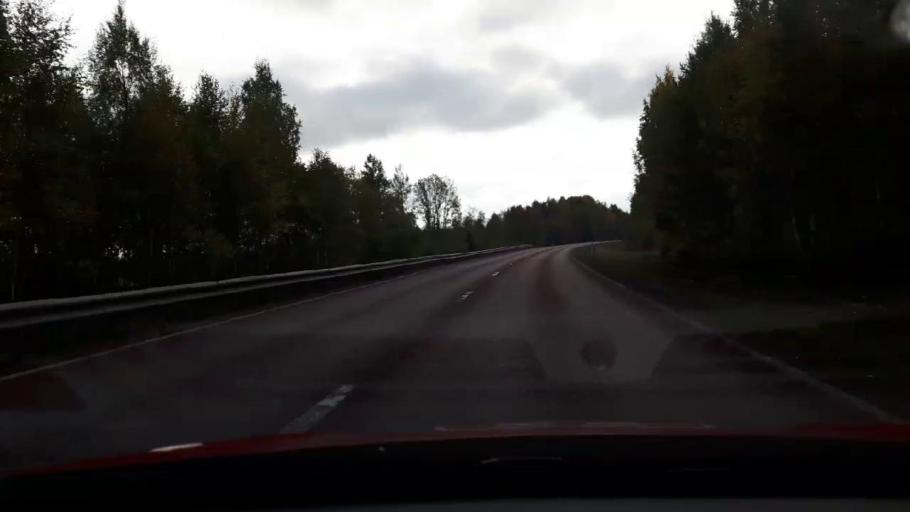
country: SE
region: Gaevleborg
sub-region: Ljusdals Kommun
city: Jaervsoe
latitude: 61.6155
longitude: 16.2948
